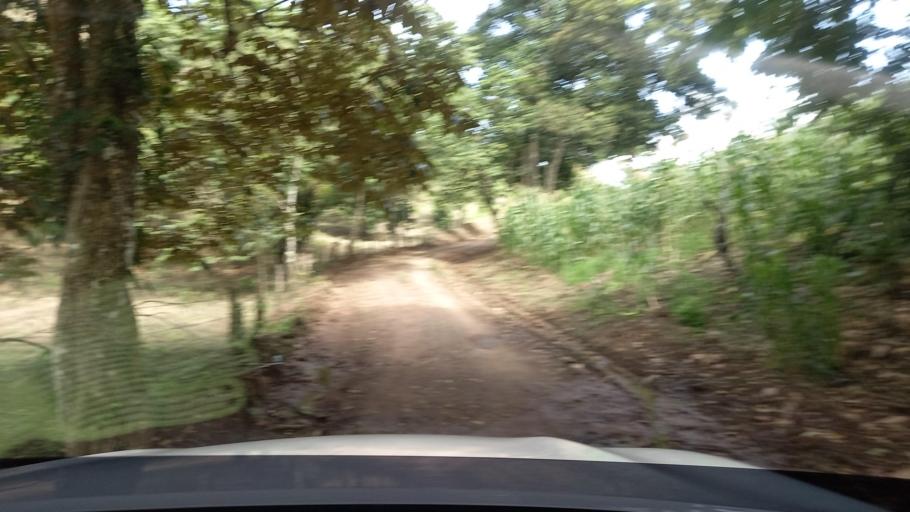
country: NI
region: Jinotega
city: San Jose de Bocay
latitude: 13.4008
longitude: -85.7000
